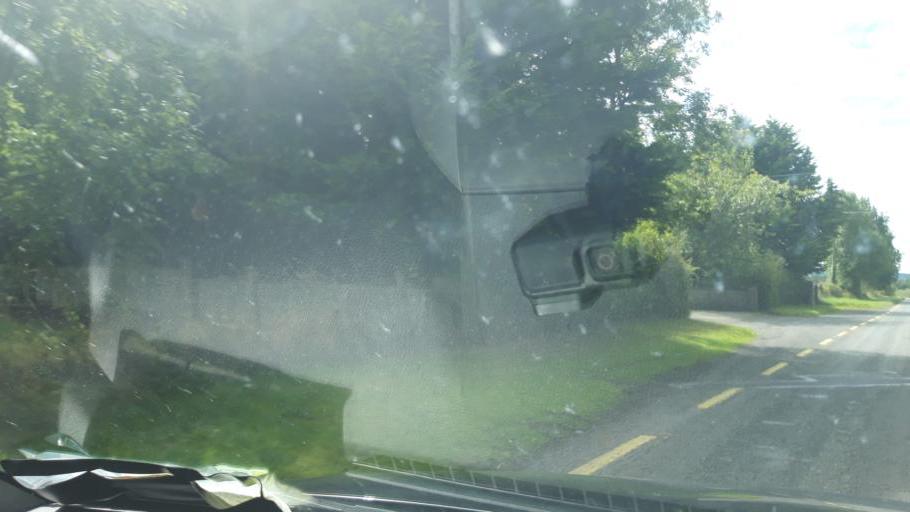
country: IE
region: Leinster
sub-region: Kilkenny
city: Callan
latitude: 52.5214
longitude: -7.4192
